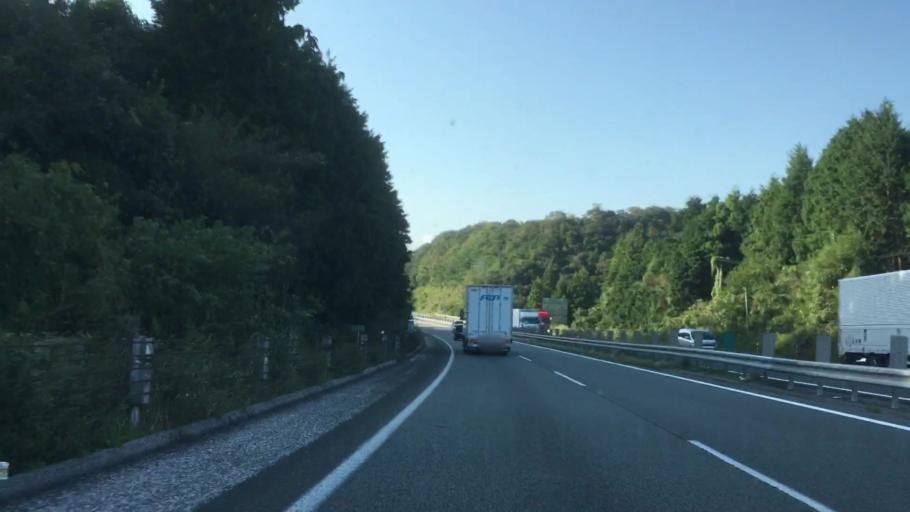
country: JP
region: Yamaguchi
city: Ogori-shimogo
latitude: 34.1594
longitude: 131.3310
